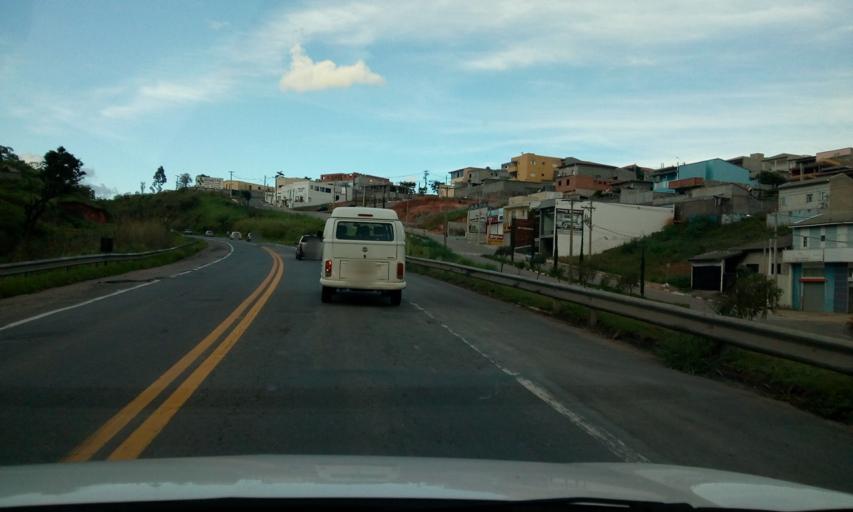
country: BR
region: Sao Paulo
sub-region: Itatiba
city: Itatiba
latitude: -23.0141
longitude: -46.8224
